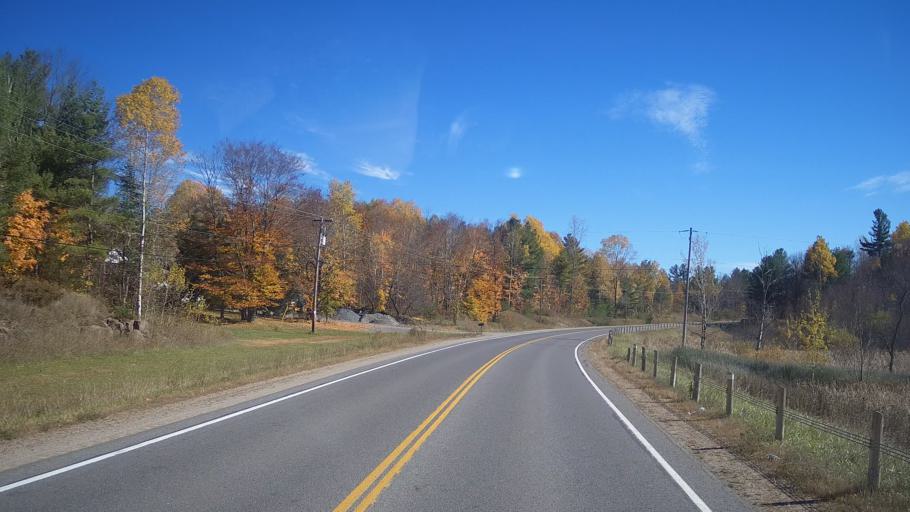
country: CA
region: Ontario
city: Skatepark
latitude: 44.6295
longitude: -76.7054
